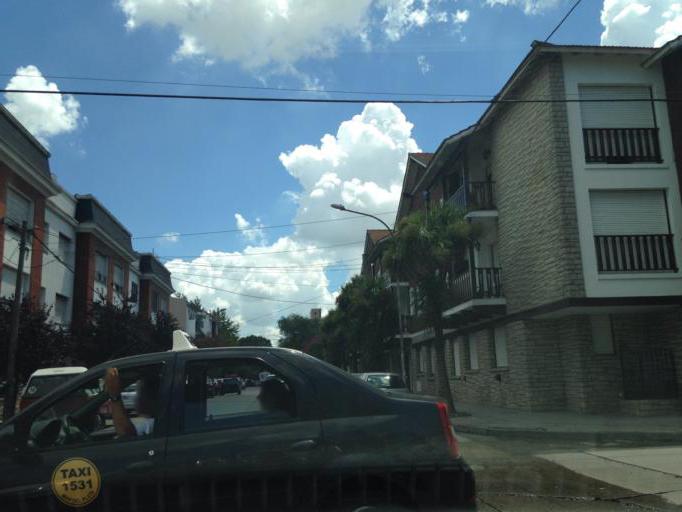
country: AR
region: Buenos Aires
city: Mar del Plata
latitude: -38.0087
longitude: -57.5598
